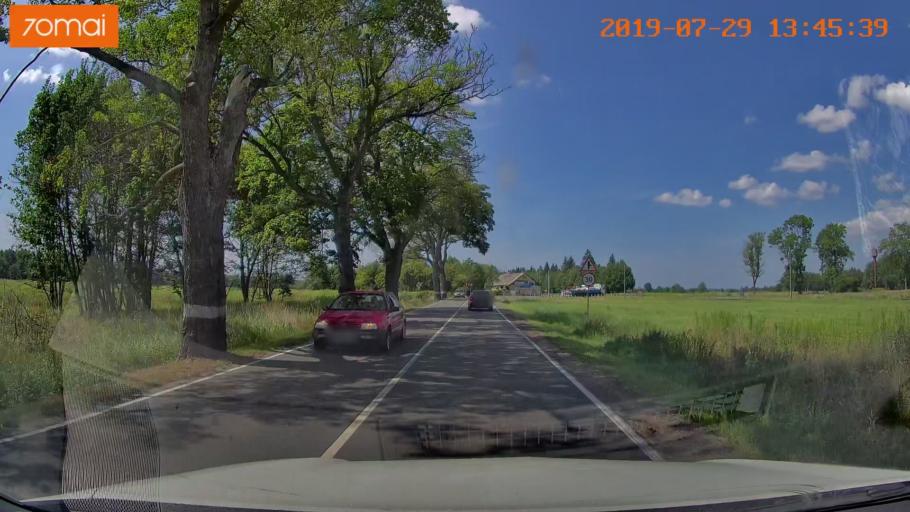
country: RU
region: Kaliningrad
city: Primorsk
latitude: 54.7398
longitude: 20.0709
